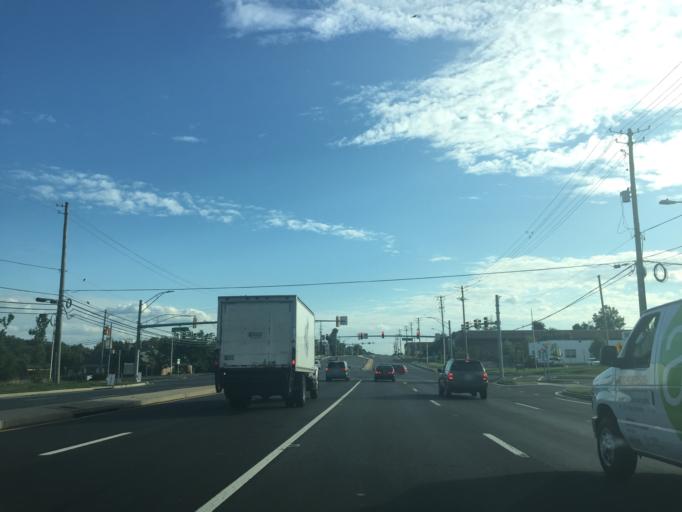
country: US
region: Maryland
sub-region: Montgomery County
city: Redland
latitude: 39.1699
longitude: -77.1540
